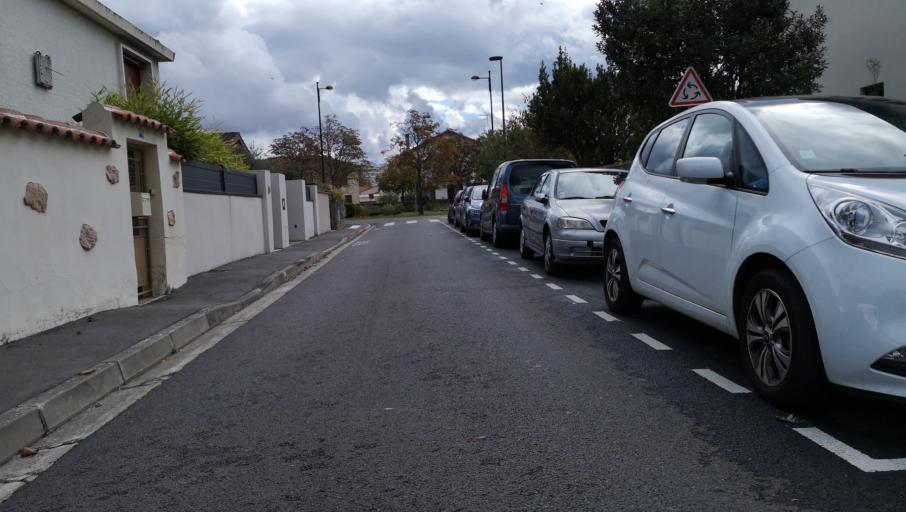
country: FR
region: Midi-Pyrenees
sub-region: Departement de la Haute-Garonne
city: Toulouse
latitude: 43.6066
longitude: 1.4126
